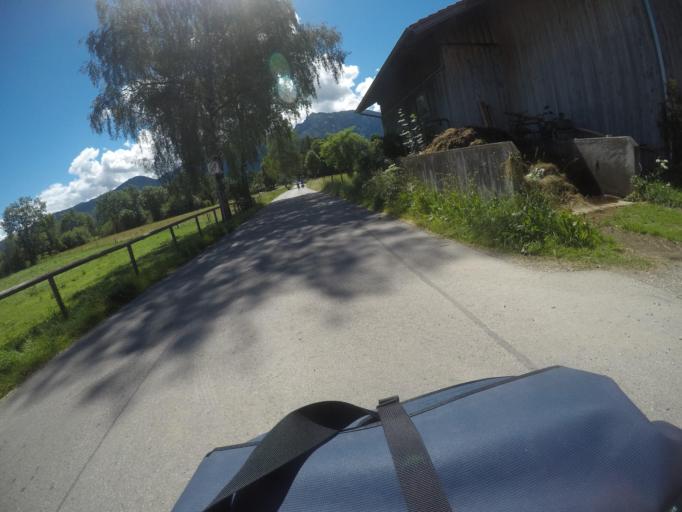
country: DE
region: Bavaria
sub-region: Swabia
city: Schwangau
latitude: 47.5930
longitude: 10.7406
